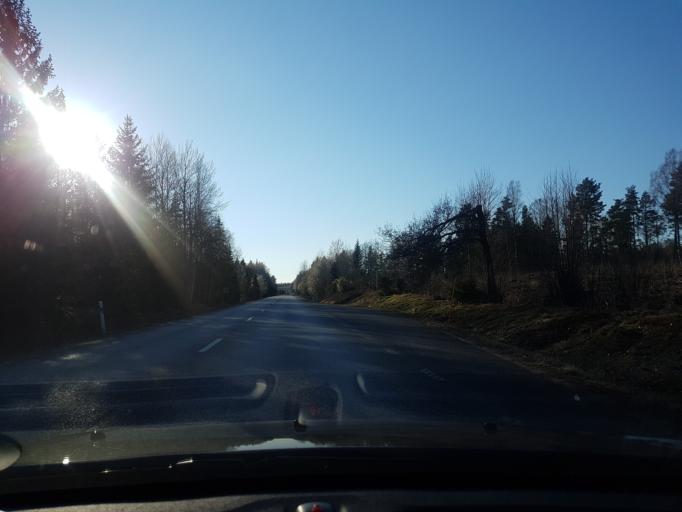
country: SE
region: Uppsala
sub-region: Enkopings Kommun
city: Orsundsbro
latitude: 59.8917
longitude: 17.1626
